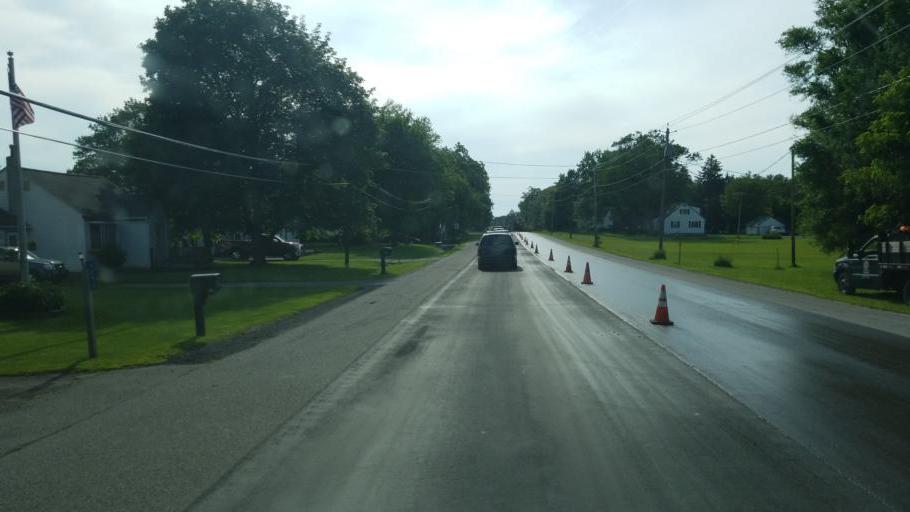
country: US
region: New York
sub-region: Genesee County
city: Le Roy
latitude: 42.9806
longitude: -78.0669
